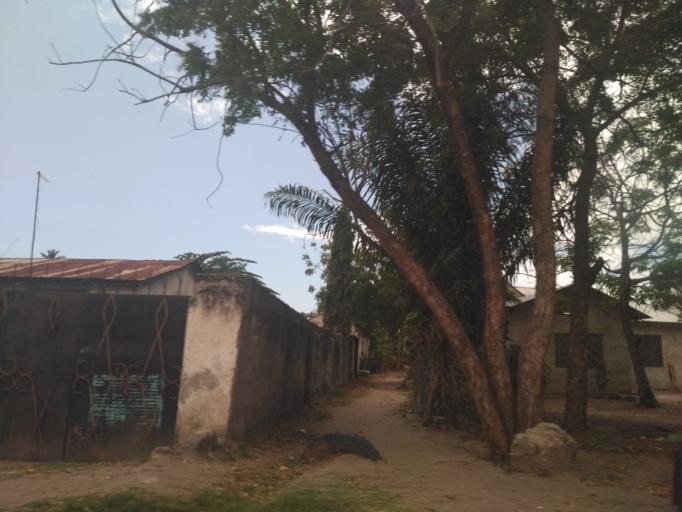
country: TZ
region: Dar es Salaam
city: Magomeni
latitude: -6.7924
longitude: 39.2706
